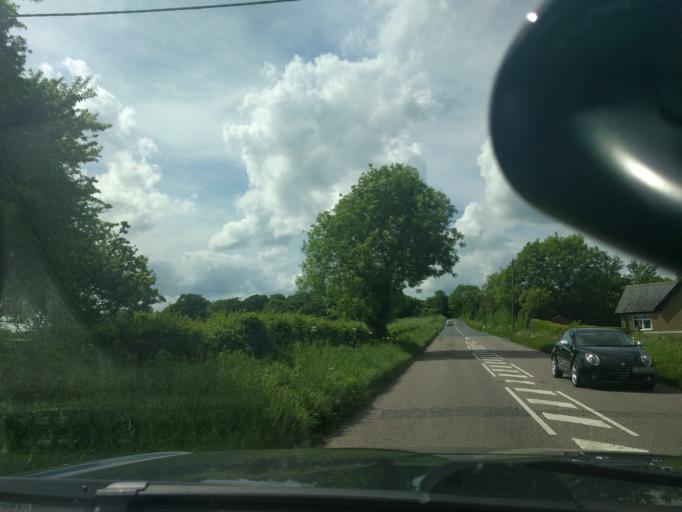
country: GB
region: England
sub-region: Wiltshire
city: Atworth
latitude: 51.3958
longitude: -2.2045
